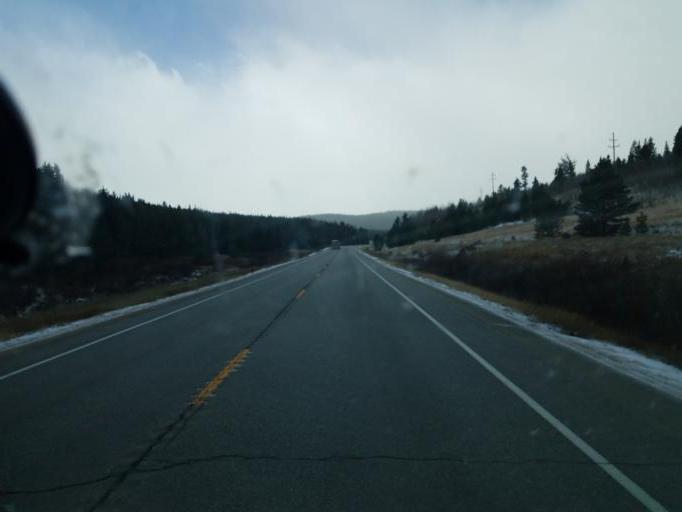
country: US
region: Colorado
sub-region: Clear Creek County
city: Georgetown
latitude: 39.4381
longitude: -105.7524
